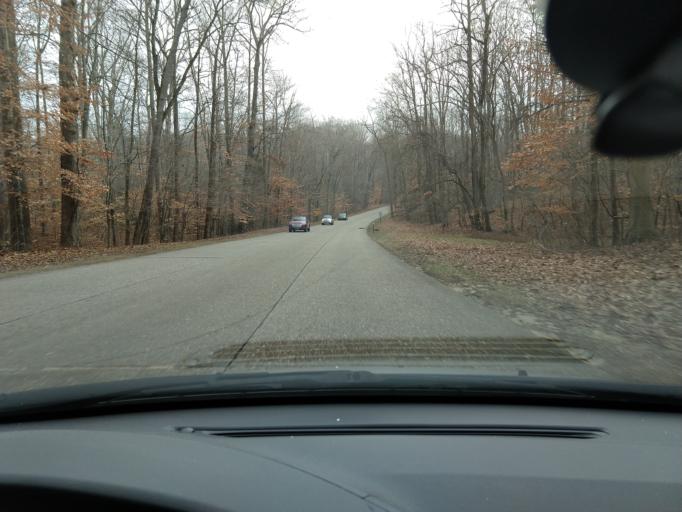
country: US
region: Virginia
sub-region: City of Williamsburg
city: Williamsburg
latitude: 37.2789
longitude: -76.6704
